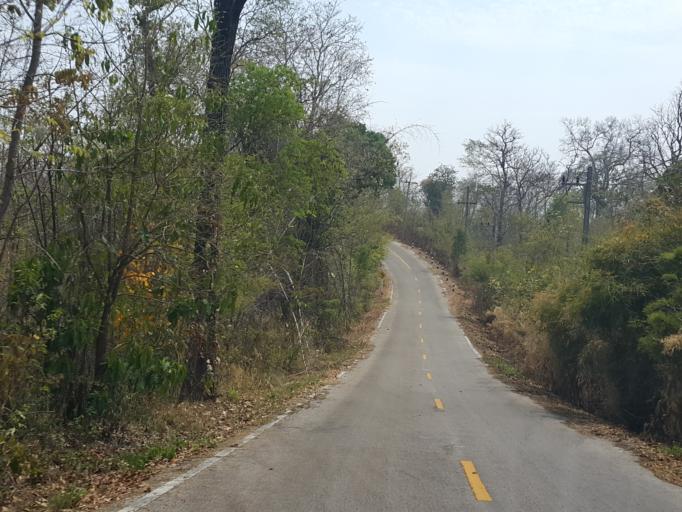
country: TH
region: Lampang
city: Mueang Pan
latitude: 18.8107
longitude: 99.4778
